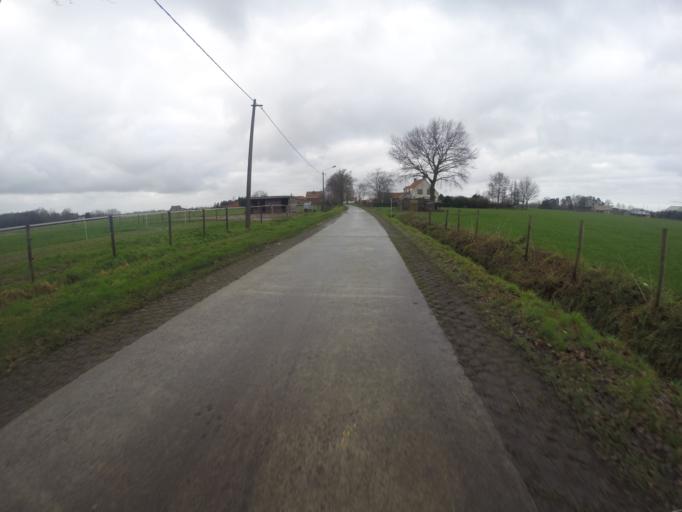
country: BE
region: Flanders
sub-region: Provincie Oost-Vlaanderen
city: Maldegem
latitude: 51.1713
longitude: 3.4954
